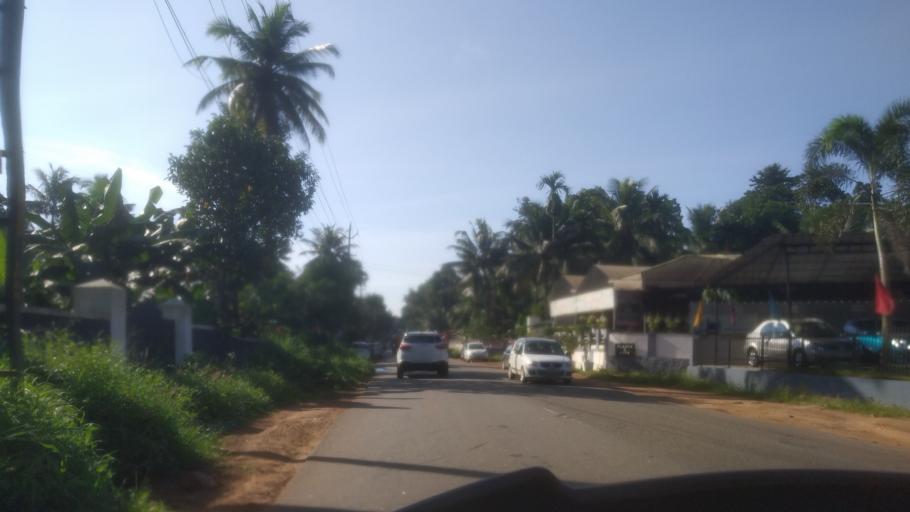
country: IN
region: Kerala
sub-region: Ernakulam
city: Muvattupuzha
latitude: 9.9774
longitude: 76.5273
